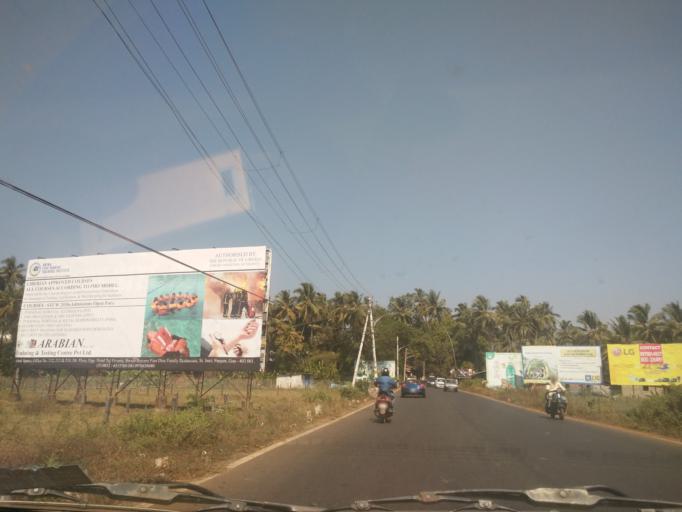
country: IN
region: Goa
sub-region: North Goa
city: Guirim
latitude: 15.5764
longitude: 73.8063
